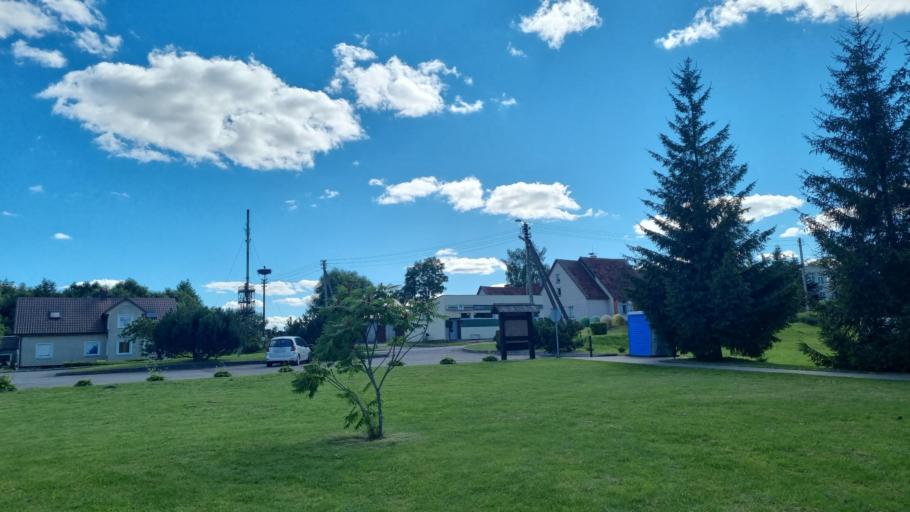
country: LT
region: Utenos apskritis
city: Visaginas
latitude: 55.5228
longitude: 26.4458
